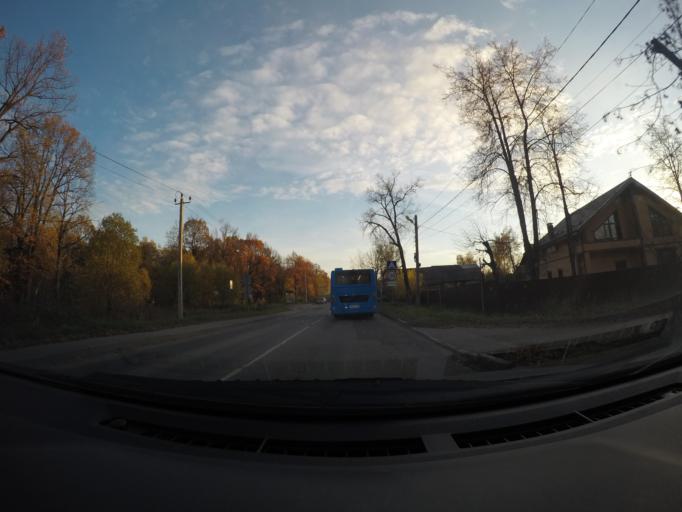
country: RU
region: Moskovskaya
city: Firsanovka
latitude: 55.9449
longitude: 37.2506
